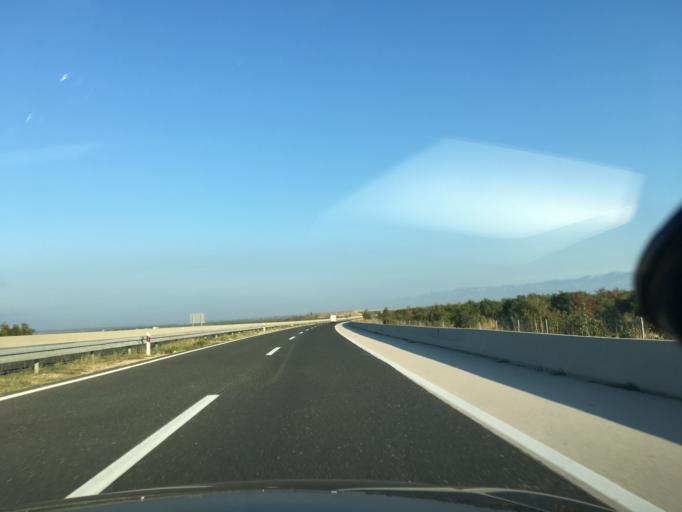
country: HR
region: Zadarska
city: Galovac
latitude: 44.1271
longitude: 15.4263
